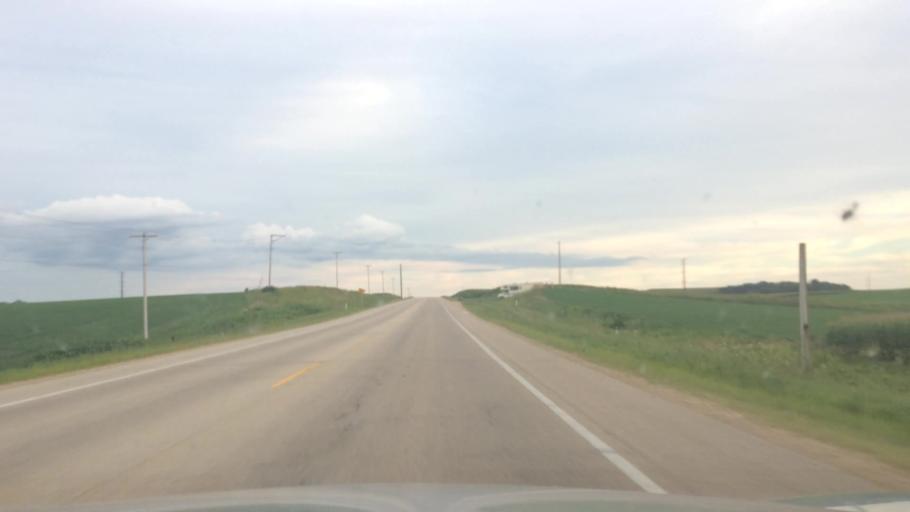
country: US
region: Wisconsin
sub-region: Columbia County
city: Lodi
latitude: 43.2648
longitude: -89.5211
